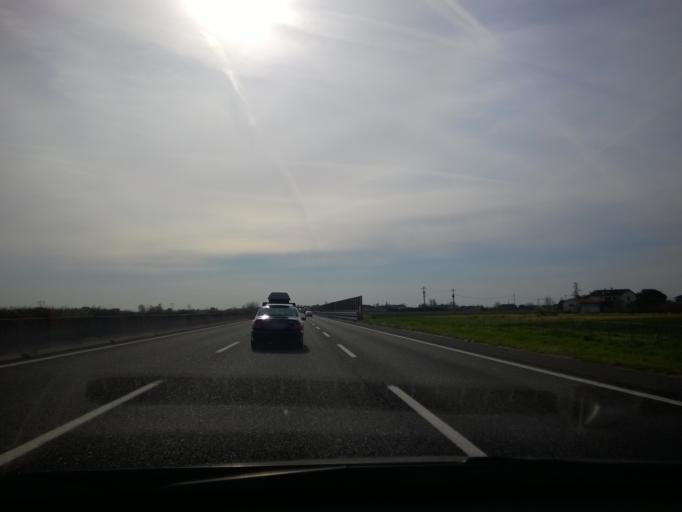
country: IT
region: Emilia-Romagna
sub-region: Forli-Cesena
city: Cesena
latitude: 44.1843
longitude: 12.2517
